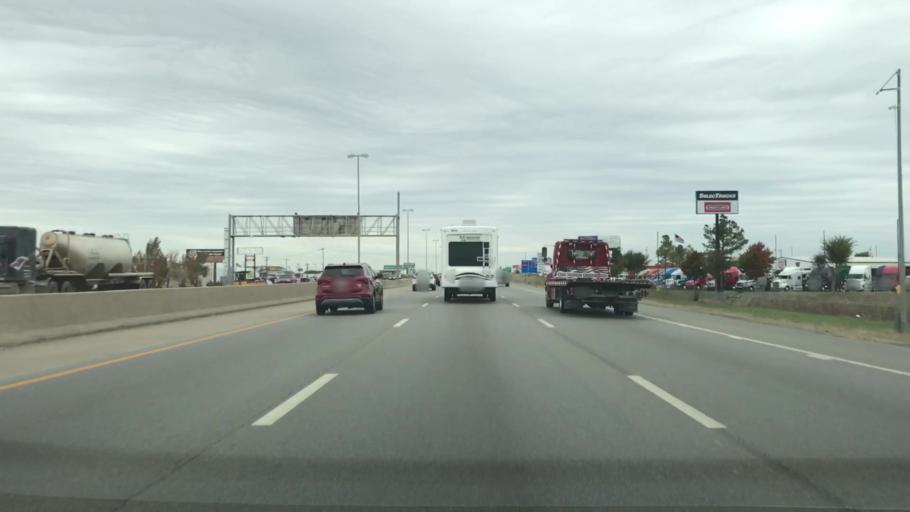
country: US
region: Oklahoma
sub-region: Oklahoma County
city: Warr Acres
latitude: 35.4602
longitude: -97.6065
